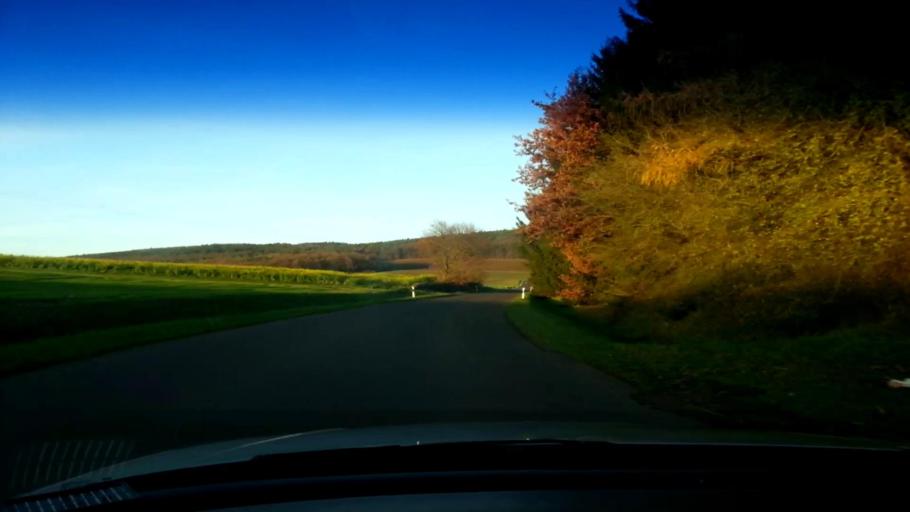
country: DE
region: Bavaria
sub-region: Upper Franconia
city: Rattelsdorf
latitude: 50.0534
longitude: 10.8869
